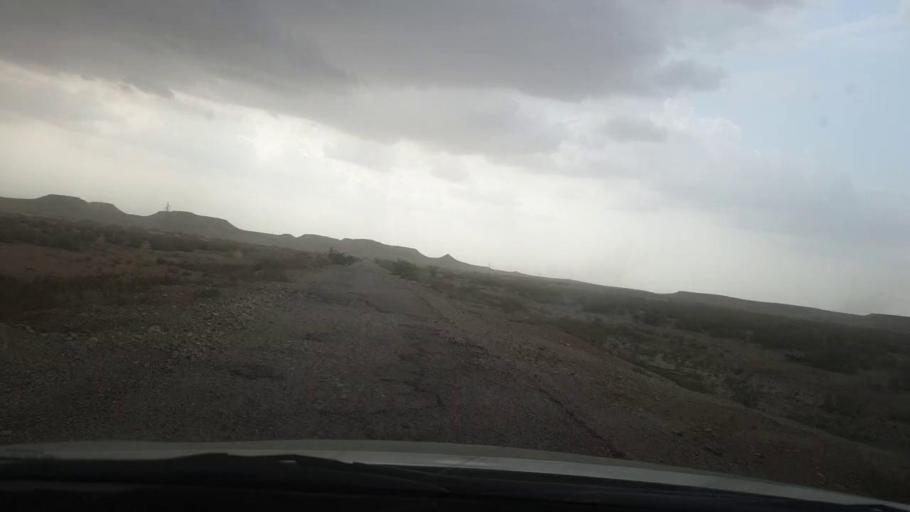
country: PK
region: Sindh
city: Khairpur
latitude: 27.4421
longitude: 68.9686
